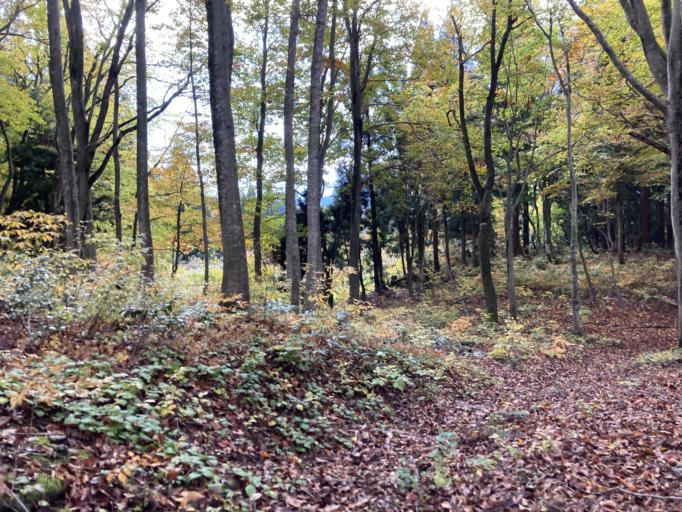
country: JP
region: Niigata
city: Tokamachi
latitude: 37.1540
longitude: 138.6274
